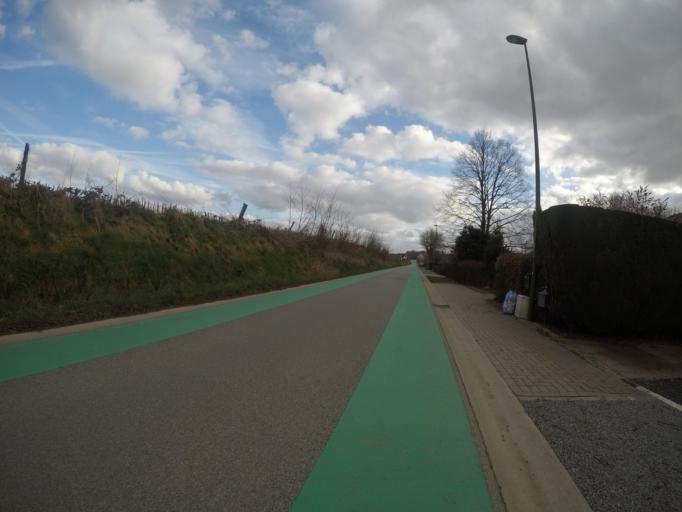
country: BE
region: Flanders
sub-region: Provincie Vlaams-Brabant
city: Pepingen
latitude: 50.7343
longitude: 4.1621
